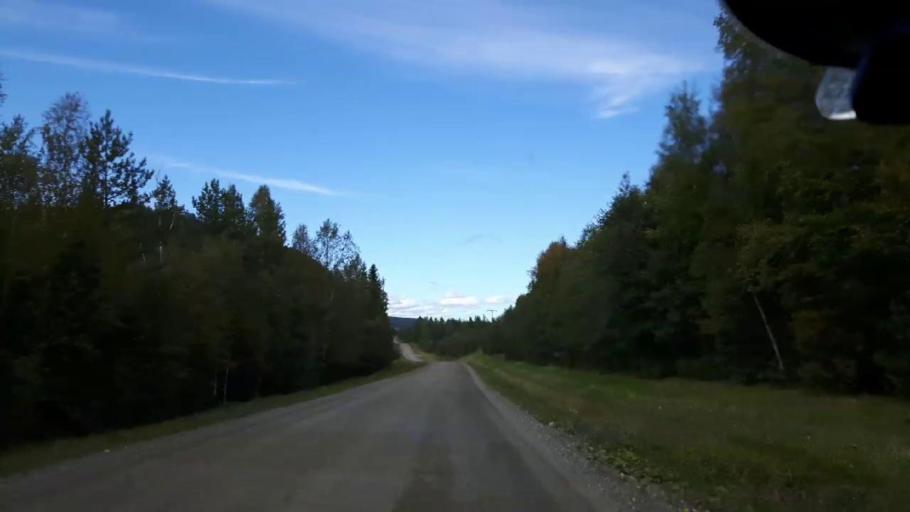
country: SE
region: Jaemtland
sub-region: Ragunda Kommun
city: Hammarstrand
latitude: 63.1244
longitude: 16.3284
